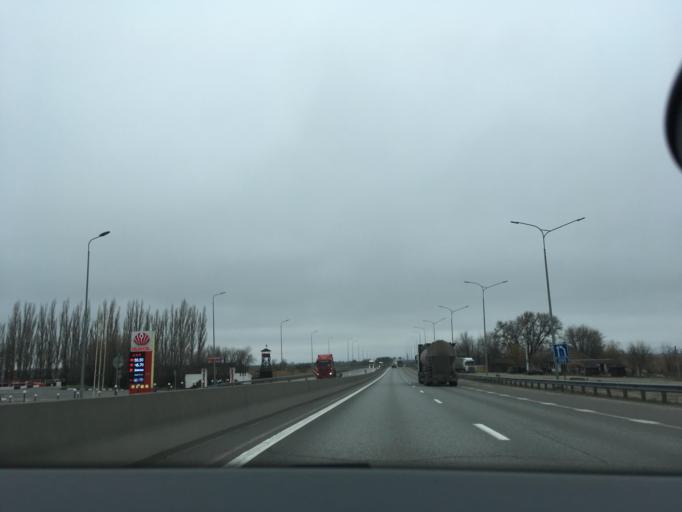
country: RU
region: Rostov
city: Samarskoye
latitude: 46.9143
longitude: 39.7061
